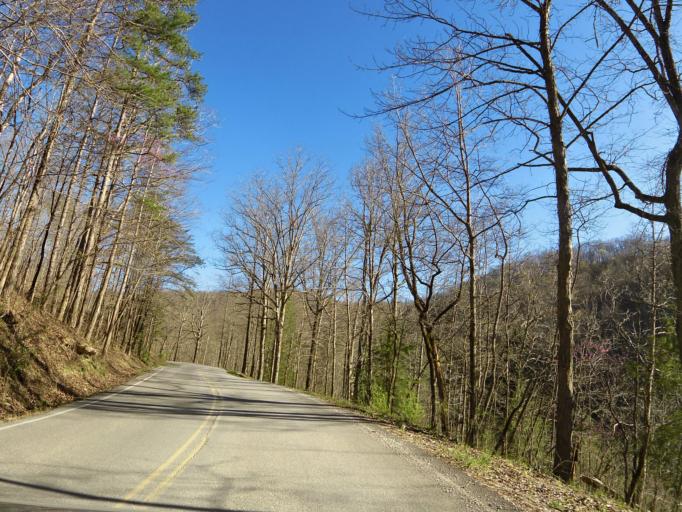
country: US
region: Tennessee
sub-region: Scott County
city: Huntsville
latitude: 36.2997
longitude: -84.3867
